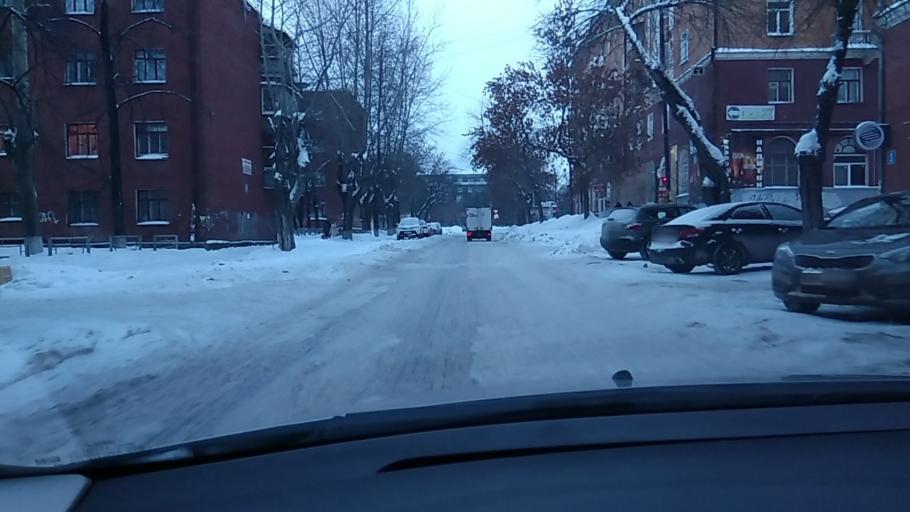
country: RU
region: Sverdlovsk
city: Yekaterinburg
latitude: 56.8905
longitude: 60.5931
